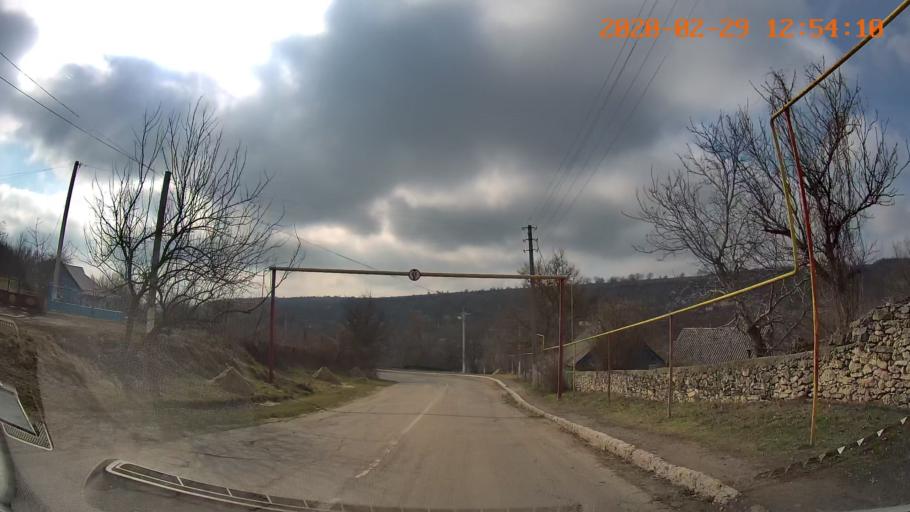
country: MD
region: Telenesti
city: Camenca
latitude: 48.1041
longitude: 28.7285
